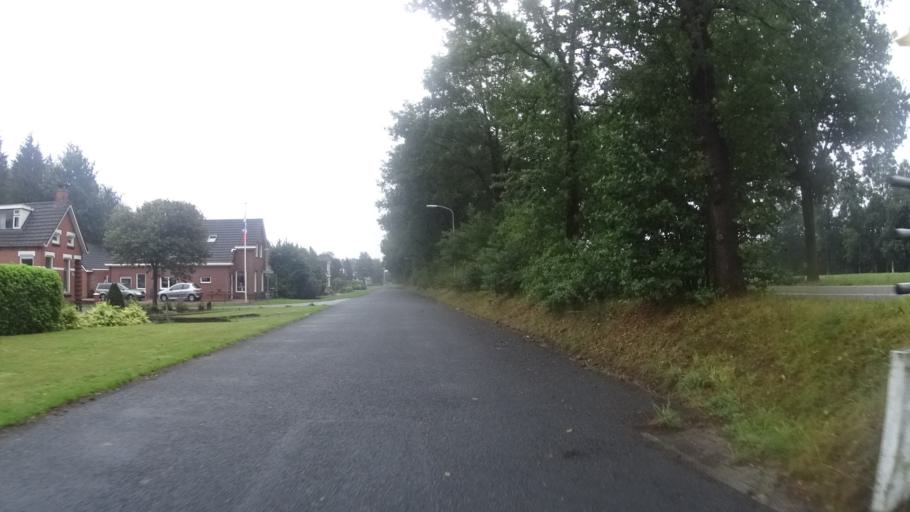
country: NL
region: Groningen
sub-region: Gemeente  Oldambt
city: Winschoten
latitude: 53.1692
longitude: 6.9880
